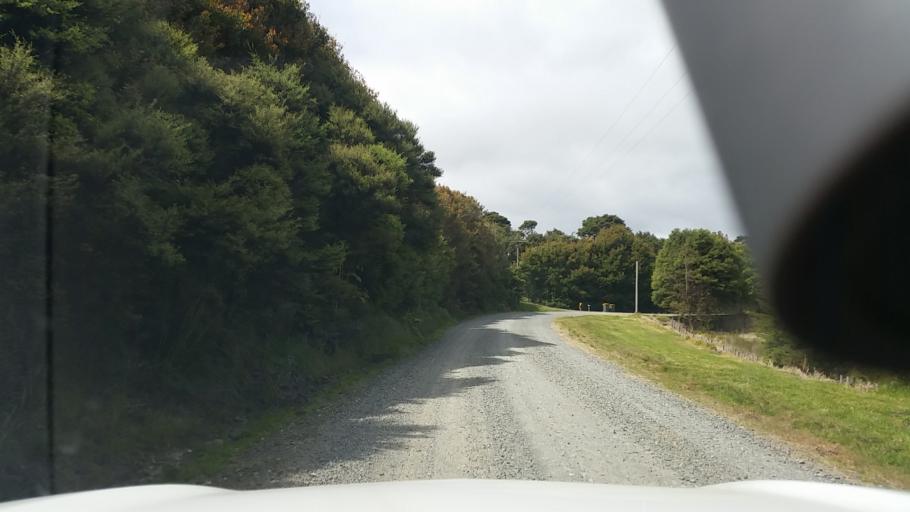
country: NZ
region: Auckland
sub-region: Auckland
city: Muriwai Beach
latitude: -36.8443
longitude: 174.5240
